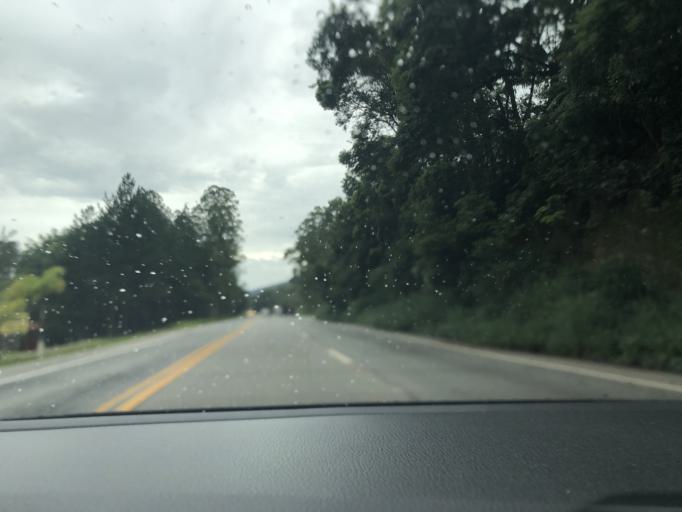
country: BR
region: Sao Paulo
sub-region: Campo Limpo Paulista
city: Campo Limpo Paulista
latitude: -23.1596
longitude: -46.7508
